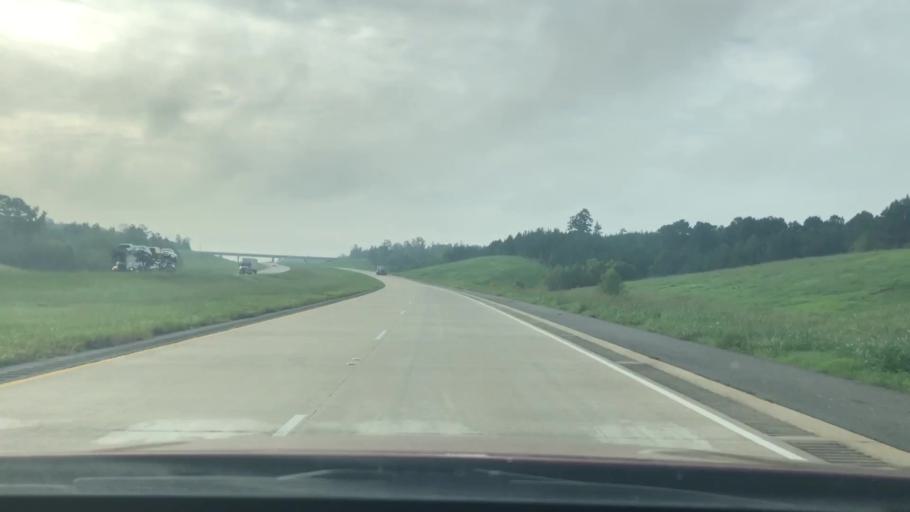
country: US
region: Louisiana
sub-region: Caddo Parish
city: Vivian
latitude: 32.9282
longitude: -93.8937
